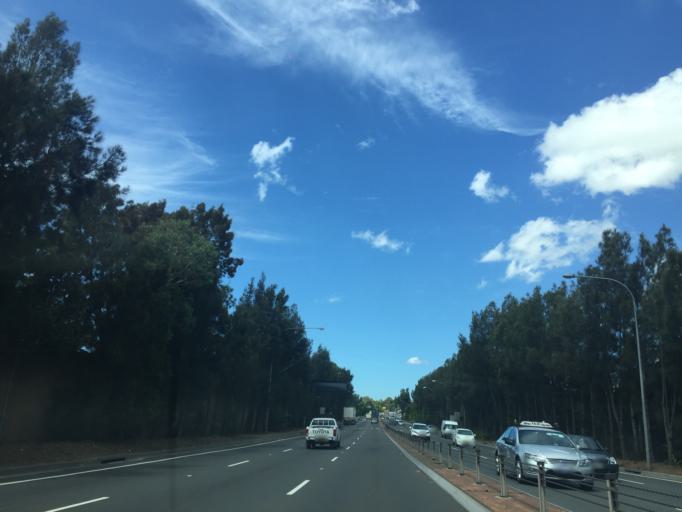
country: AU
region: New South Wales
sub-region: Strathfield
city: Homebush
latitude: -33.8788
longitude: 151.0683
